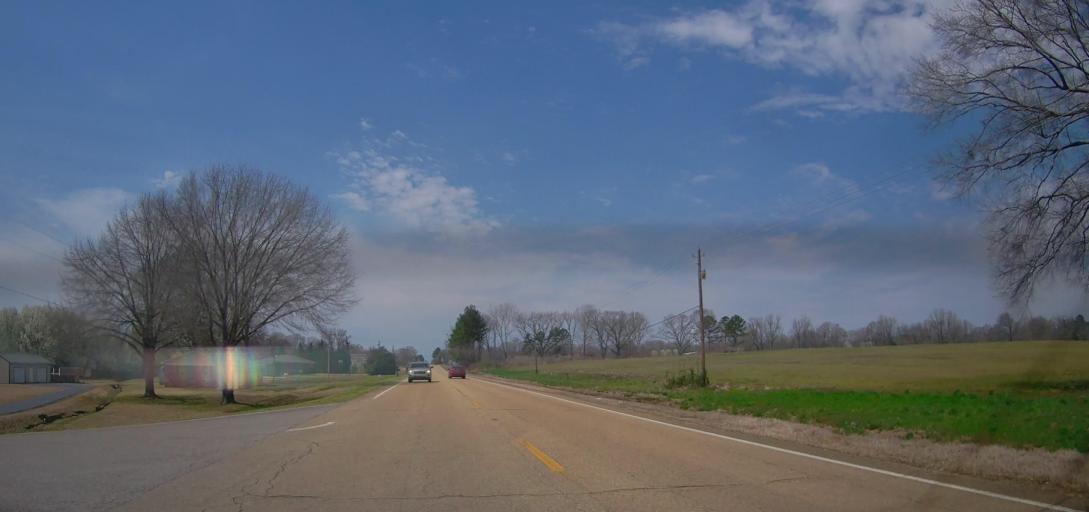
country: US
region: Mississippi
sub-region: Union County
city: New Albany
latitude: 34.6175
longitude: -89.1798
